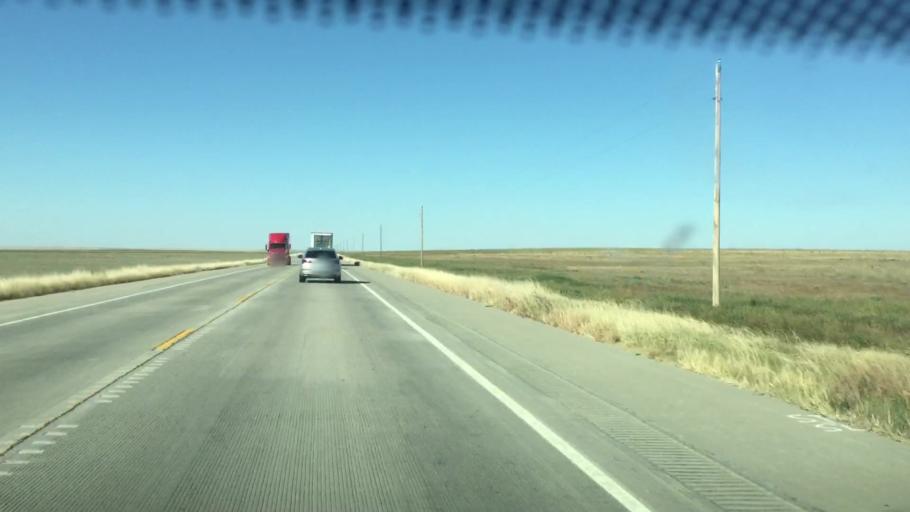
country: US
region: Colorado
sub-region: Kiowa County
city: Eads
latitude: 38.3033
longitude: -102.7199
